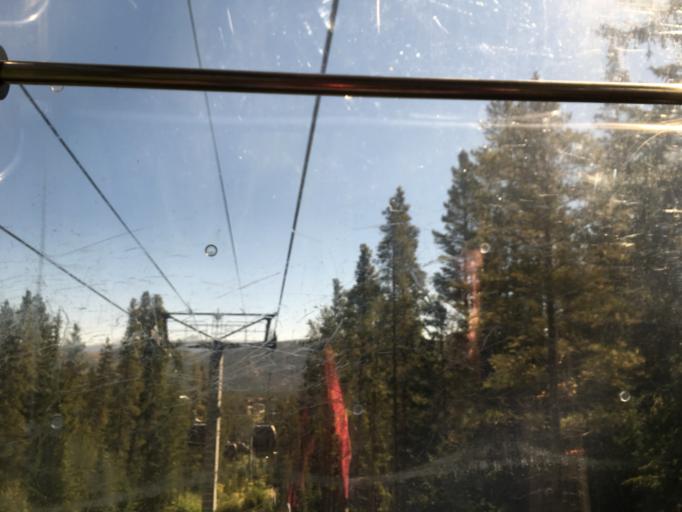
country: US
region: Colorado
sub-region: Summit County
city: Breckenridge
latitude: 39.4856
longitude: -106.0646
